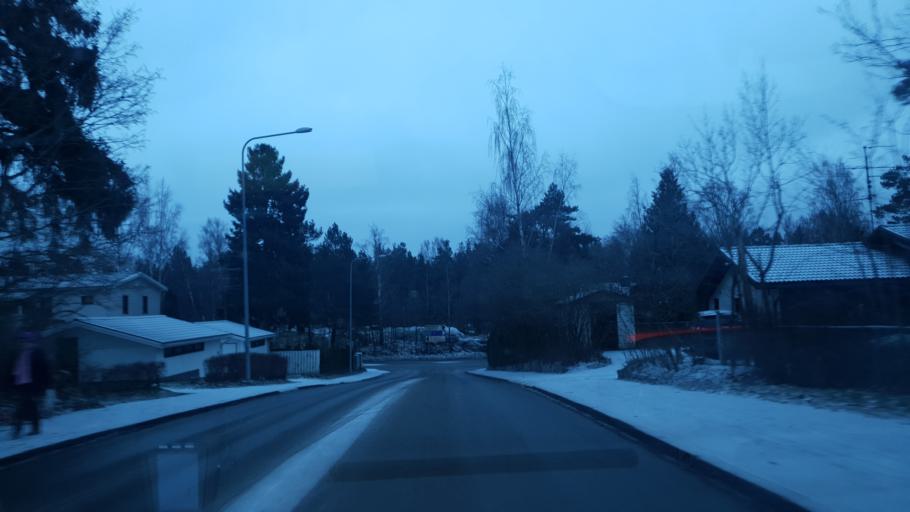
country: FI
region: Uusimaa
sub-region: Helsinki
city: Vantaa
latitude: 60.2448
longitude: 25.0351
